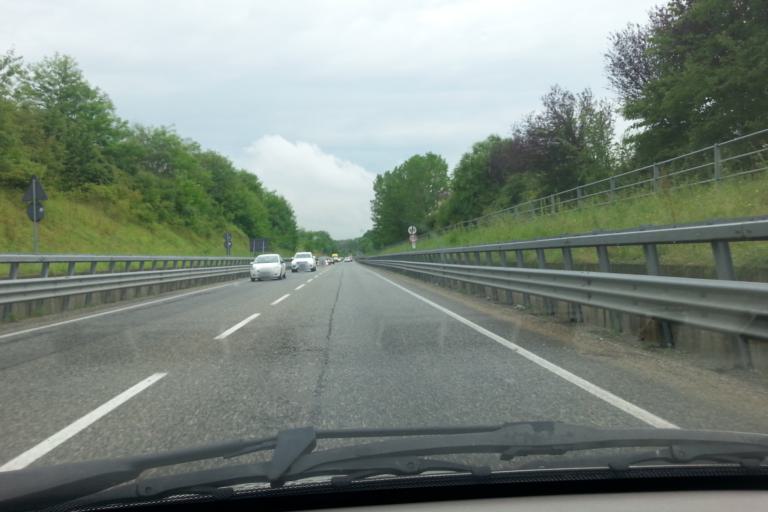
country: IT
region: Piedmont
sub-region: Provincia di Torino
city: Pasta
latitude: 45.0307
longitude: 7.5536
